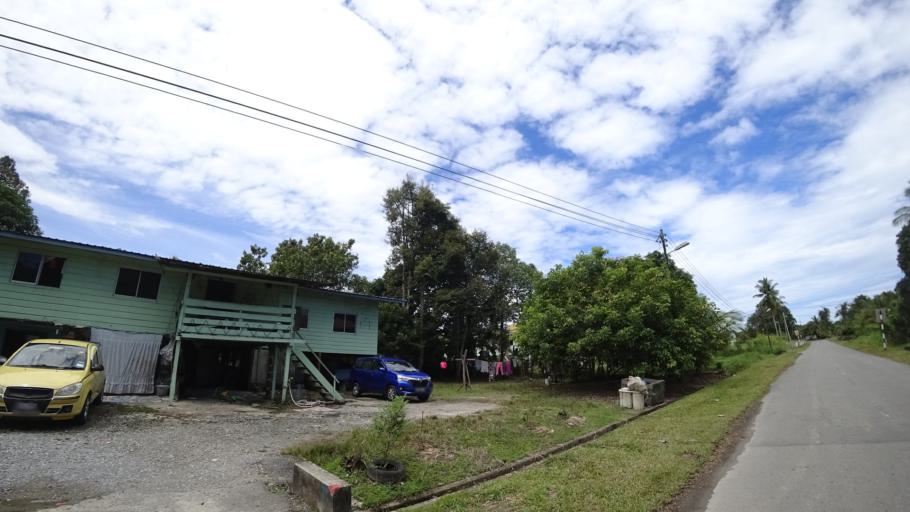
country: BN
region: Tutong
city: Tutong
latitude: 4.7697
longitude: 114.8197
